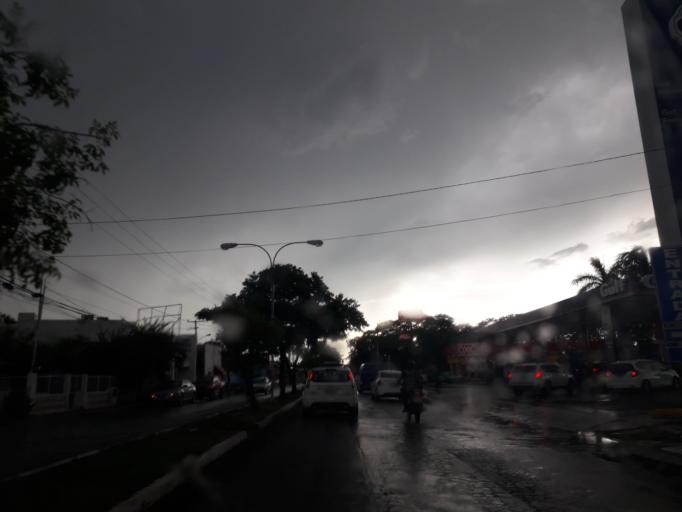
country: MX
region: Yucatan
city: Merida
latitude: 20.9794
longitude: -89.6472
